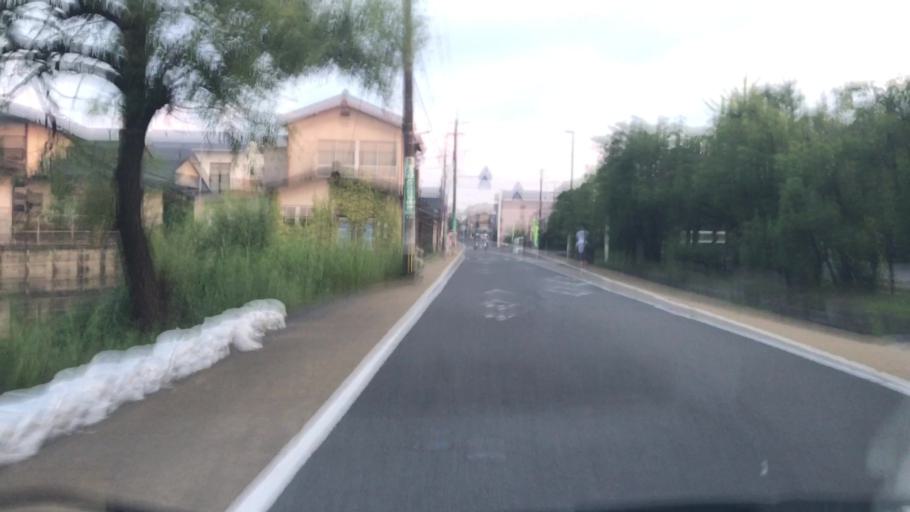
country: JP
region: Saga Prefecture
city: Saga-shi
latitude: 33.2500
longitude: 130.2807
